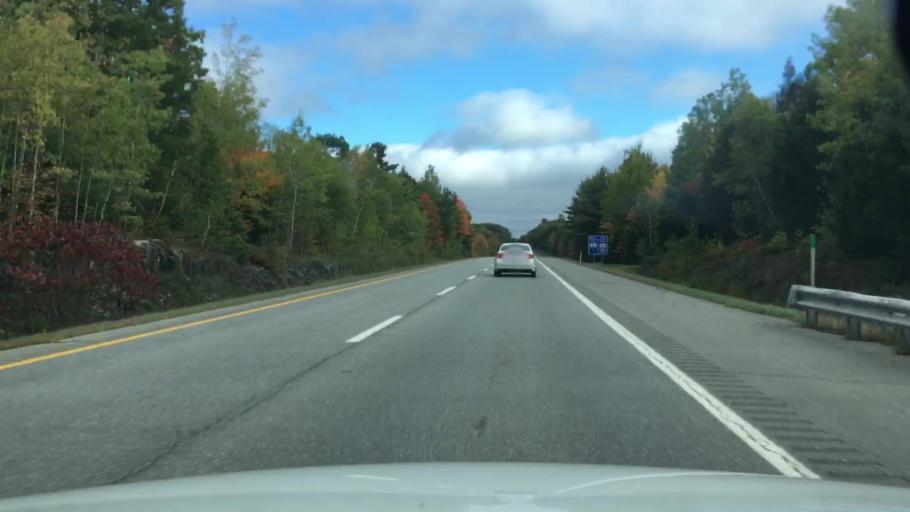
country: US
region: Maine
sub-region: Penobscot County
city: Carmel
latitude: 44.7659
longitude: -68.9937
